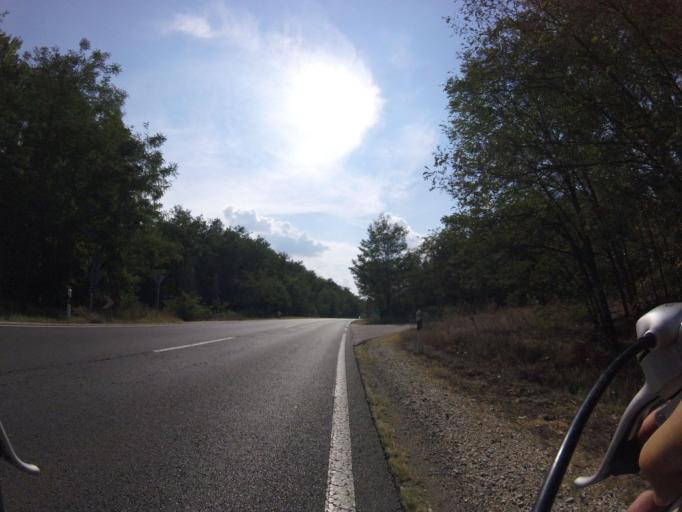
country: HU
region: Szabolcs-Szatmar-Bereg
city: Nyirbogdany
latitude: 48.0524
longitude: 21.9019
